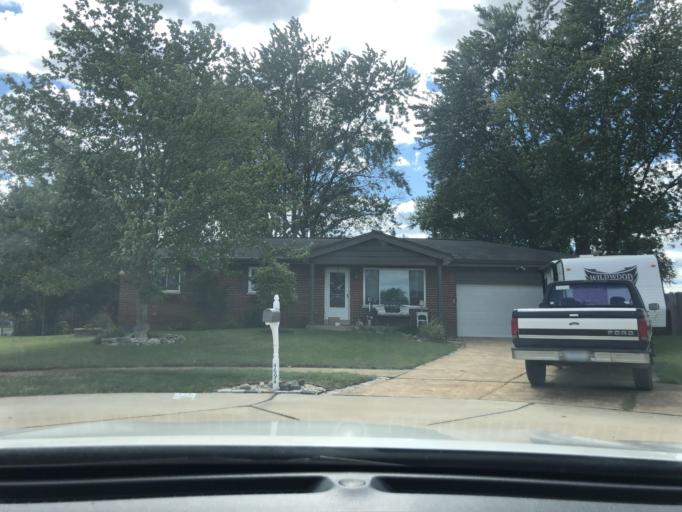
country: US
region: Missouri
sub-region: Saint Louis County
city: Concord
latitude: 38.4998
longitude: -90.3587
